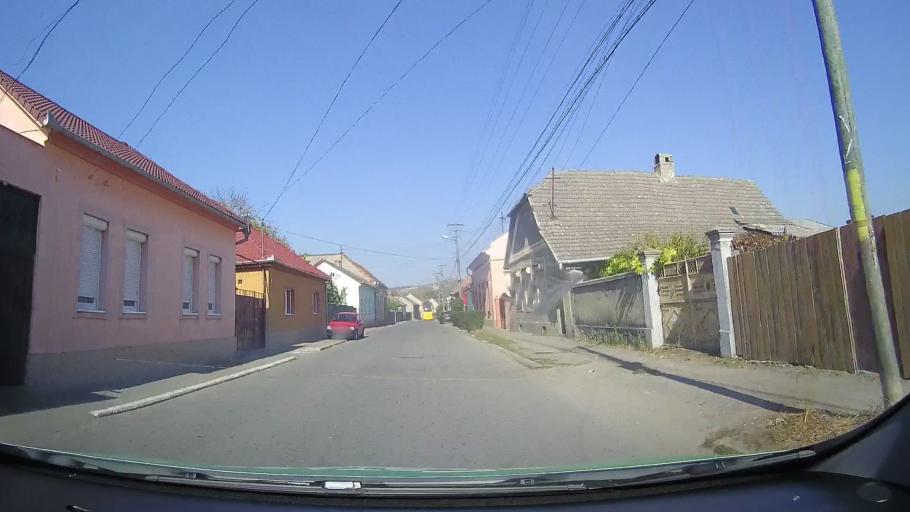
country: RO
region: Arad
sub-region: Oras Lipova
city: Lipova
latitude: 46.0878
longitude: 21.6910
